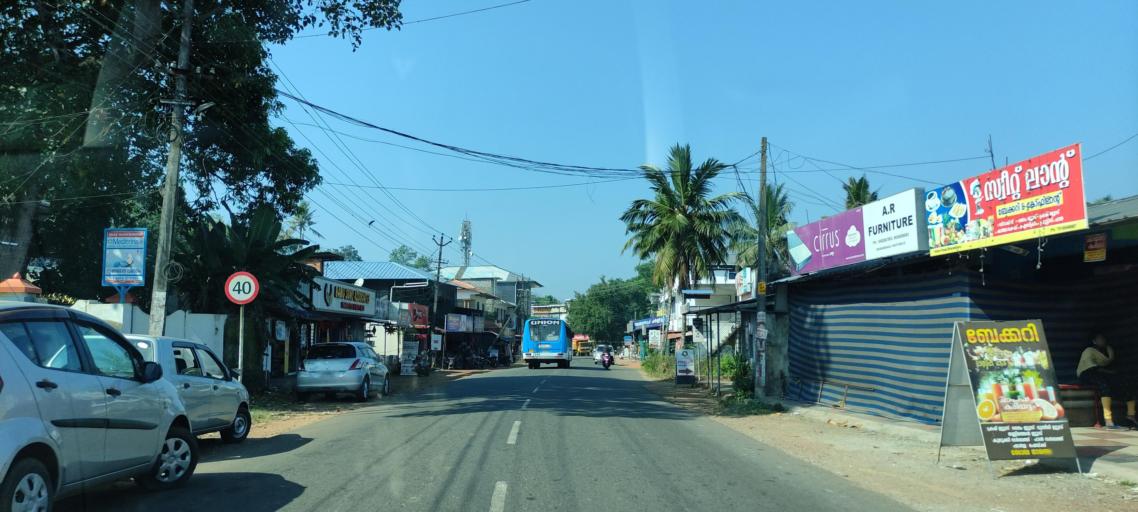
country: IN
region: Kerala
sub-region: Kollam
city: Panmana
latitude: 9.0618
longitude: 76.6403
